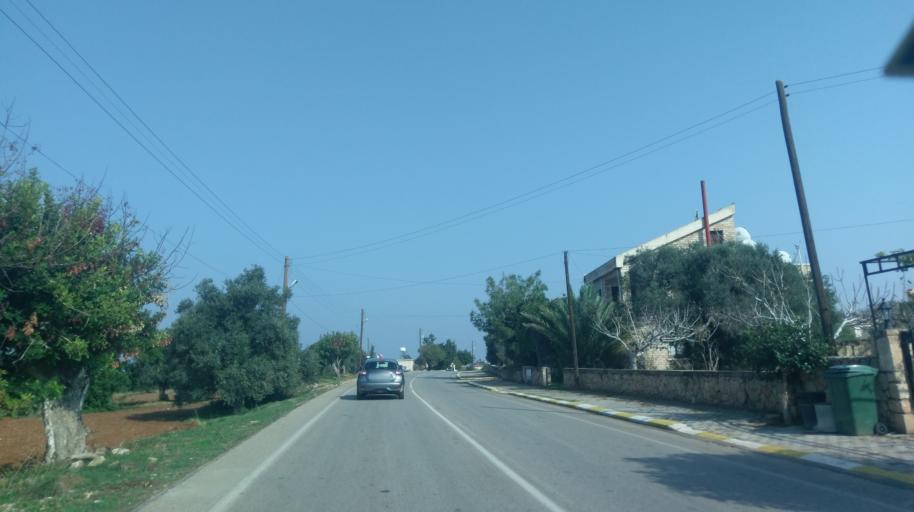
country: CY
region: Ammochostos
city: Leonarisso
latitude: 35.5240
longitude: 34.1766
